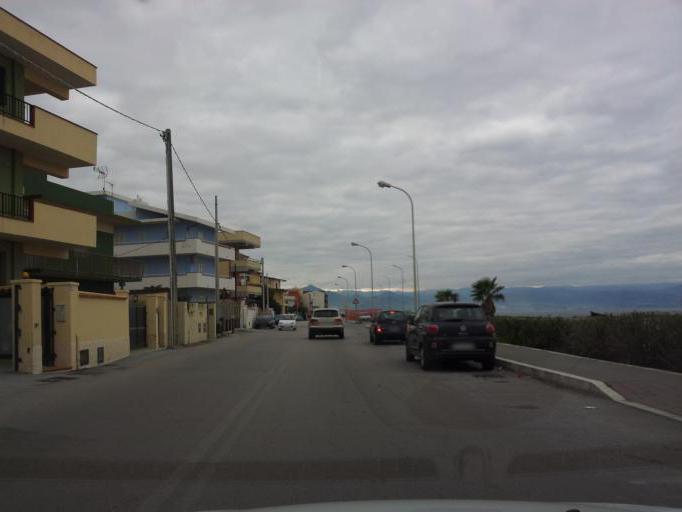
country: IT
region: Sicily
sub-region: Messina
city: Milazzo
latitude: 38.2115
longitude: 15.2298
